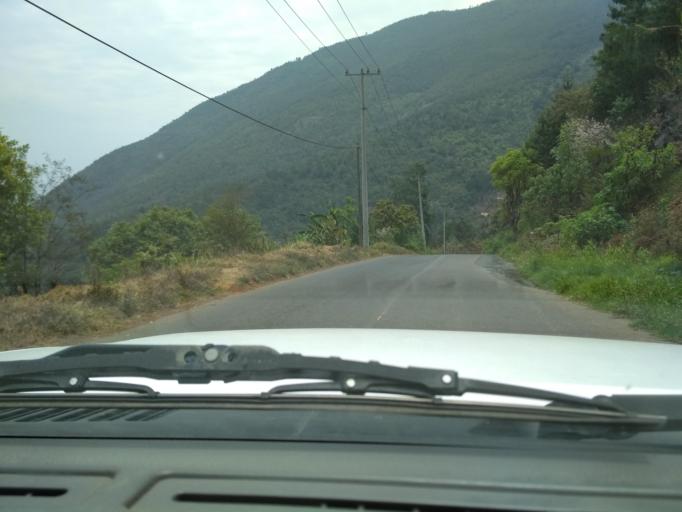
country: MX
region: Veracruz
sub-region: Camerino Z. Mendoza
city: La Cuesta
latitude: 18.7875
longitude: -97.1659
